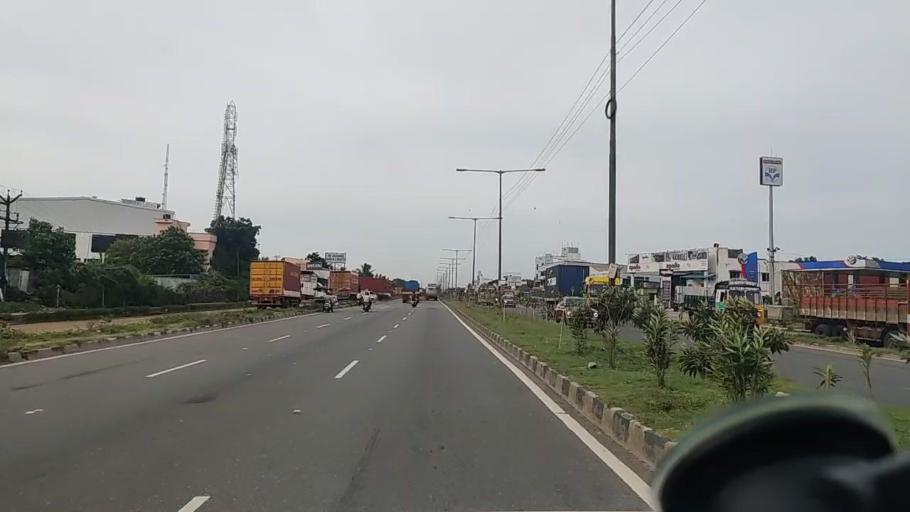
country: IN
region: Tamil Nadu
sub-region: Thiruvallur
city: Chinnasekkadu
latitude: 13.1538
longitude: 80.2240
